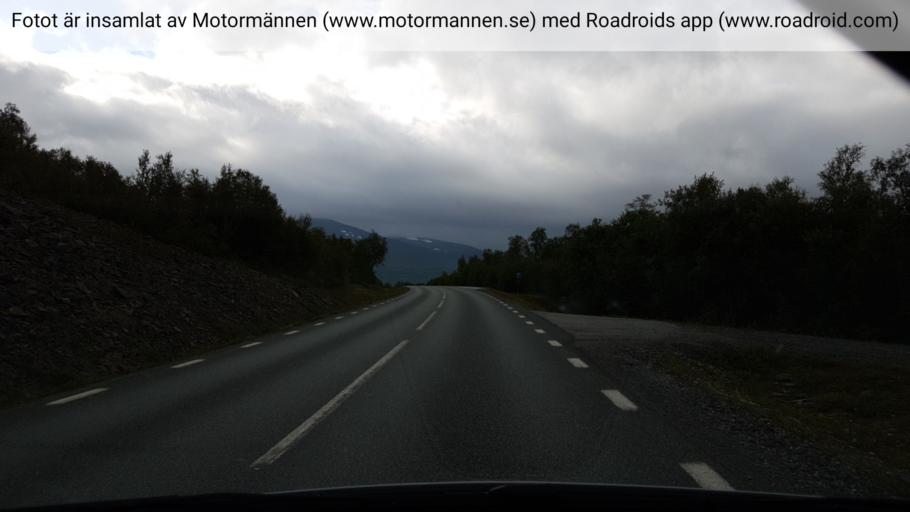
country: NO
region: Nordland
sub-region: Rana
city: Mo i Rana
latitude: 66.0639
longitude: 14.8725
